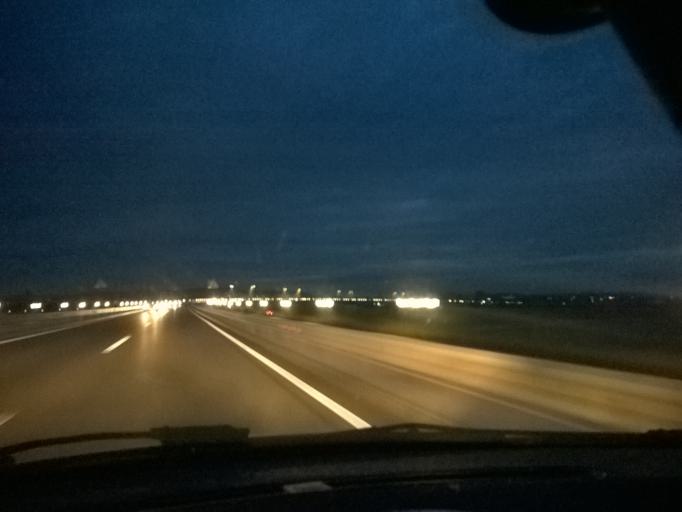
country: SI
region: Ptuj
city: Ptuj
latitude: 46.4094
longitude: 15.8769
